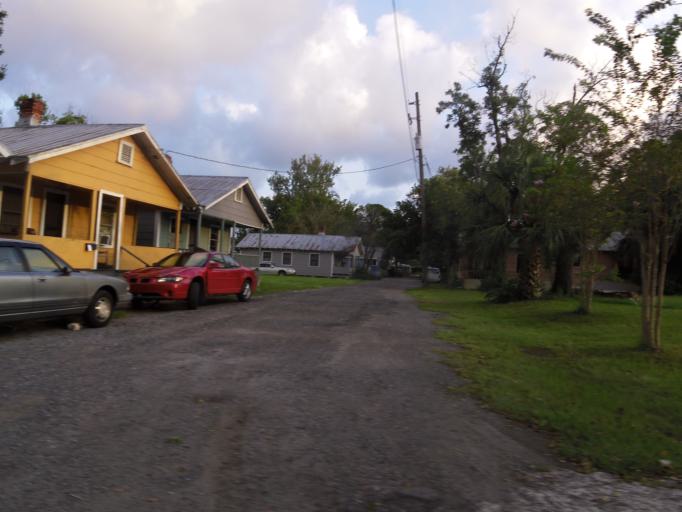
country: US
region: Florida
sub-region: Duval County
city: Jacksonville
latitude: 30.3241
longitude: -81.6849
